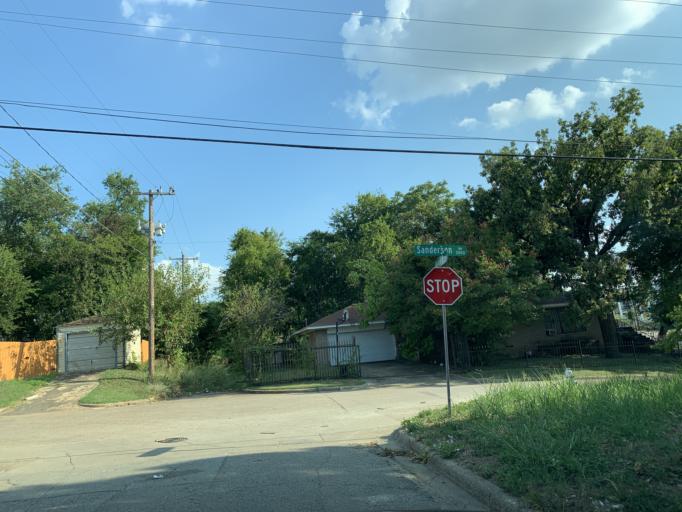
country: US
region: Texas
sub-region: Dallas County
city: Dallas
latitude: 32.7430
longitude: -96.7942
